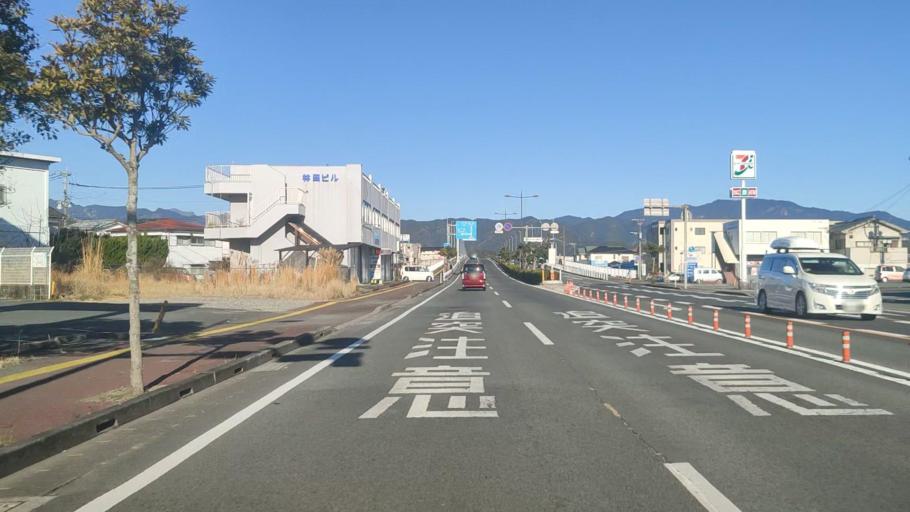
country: JP
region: Miyazaki
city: Nobeoka
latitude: 32.5797
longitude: 131.6823
